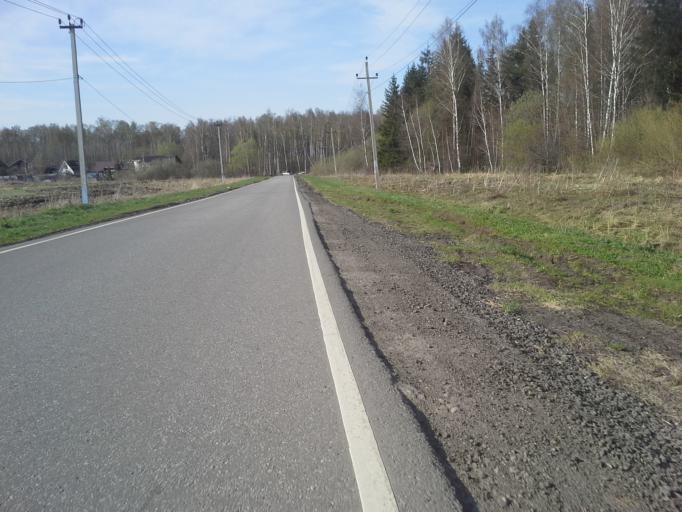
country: RU
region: Moskovskaya
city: Vatutinki
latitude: 55.4678
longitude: 37.3808
